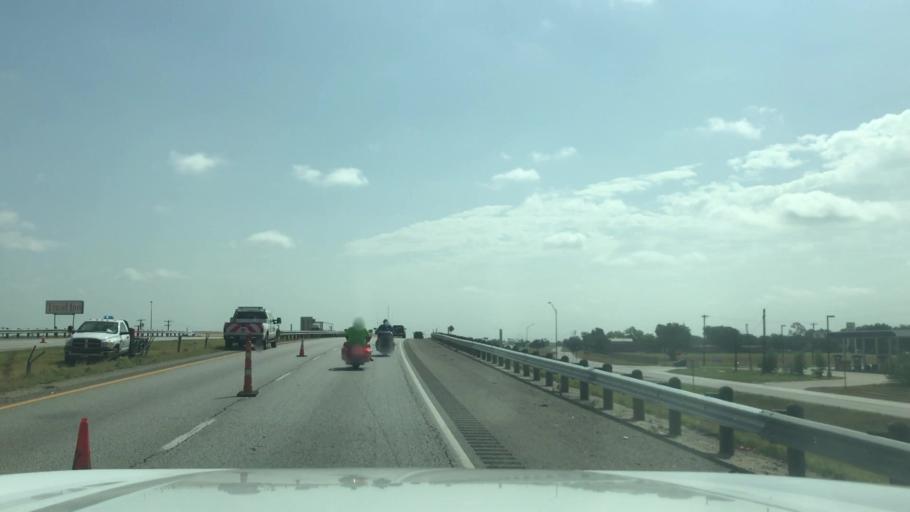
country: US
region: Texas
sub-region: Taylor County
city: Abilene
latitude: 32.4900
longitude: -99.7498
